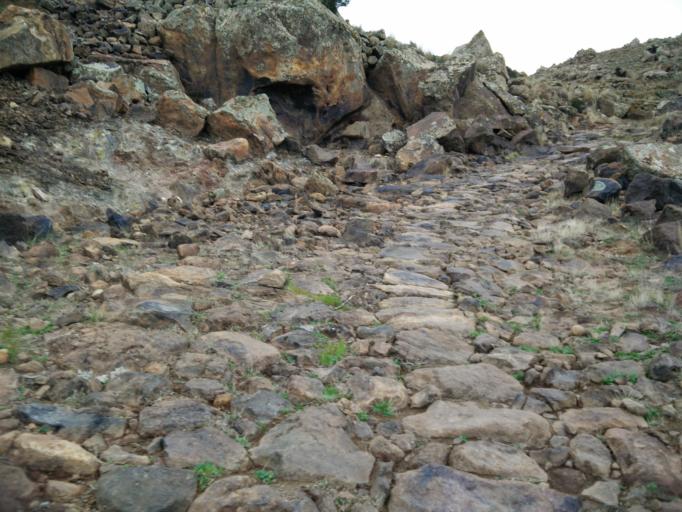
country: IT
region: Sicily
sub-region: Trapani
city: Kamma
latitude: 36.7670
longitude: 11.9977
